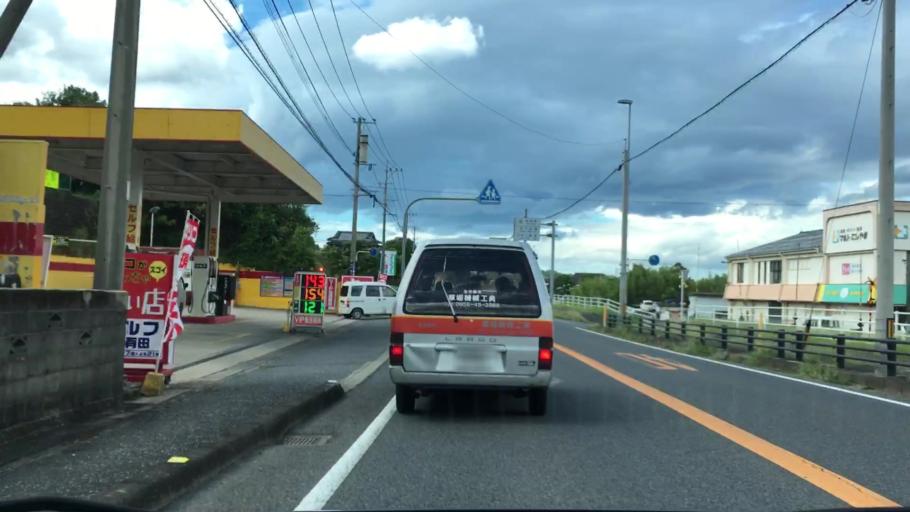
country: JP
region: Saga Prefecture
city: Imaricho-ko
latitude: 33.2067
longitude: 129.8505
